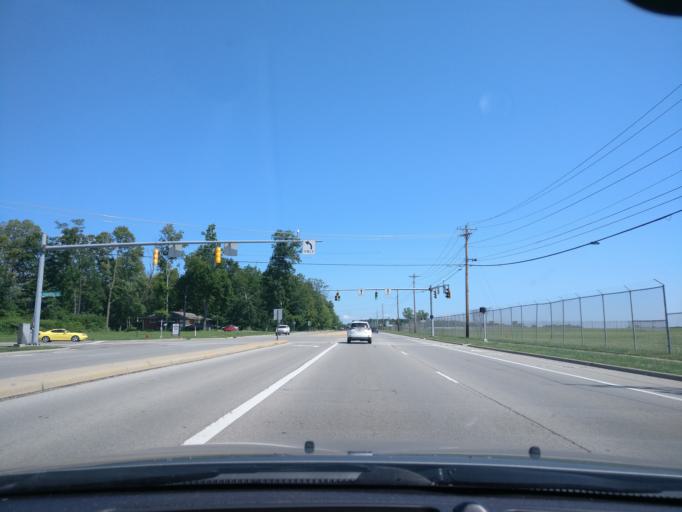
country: US
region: Ohio
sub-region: Warren County
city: Springboro
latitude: 39.5822
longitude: -84.2304
